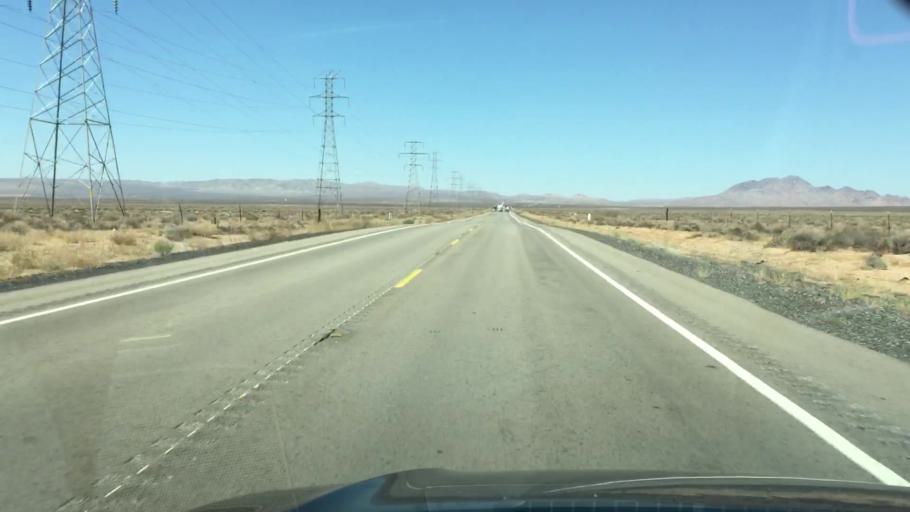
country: US
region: California
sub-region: Kern County
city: Boron
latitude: 35.1882
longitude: -117.5968
